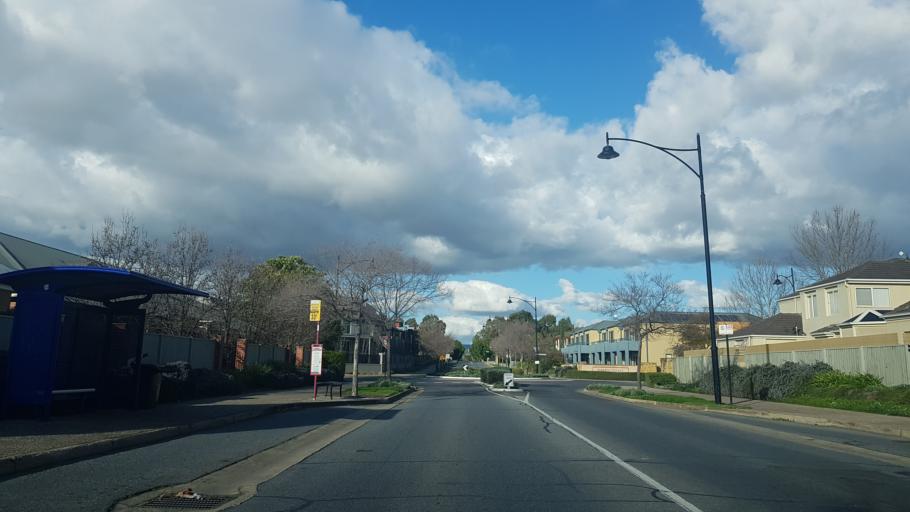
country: AU
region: South Australia
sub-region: Salisbury
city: Ingle Farm
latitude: -34.8110
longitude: 138.6103
